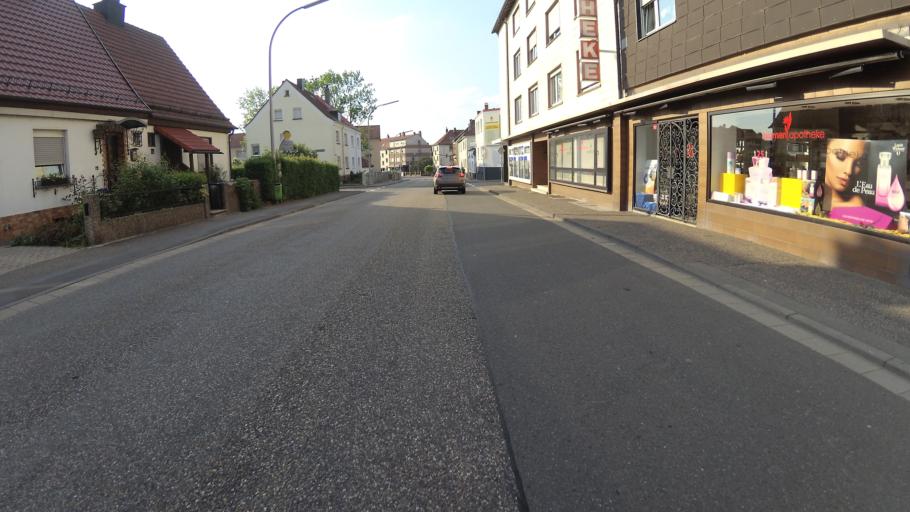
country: DE
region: Rheinland-Pfalz
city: Pirmasens
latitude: 49.1936
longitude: 7.5958
